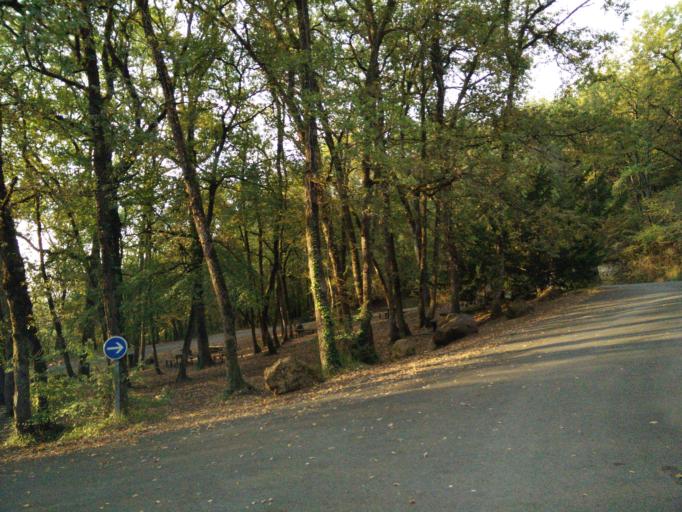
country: FR
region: Aquitaine
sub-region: Departement de la Dordogne
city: Rouffignac-Saint-Cernin-de-Reilhac
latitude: 45.0079
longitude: 0.9879
